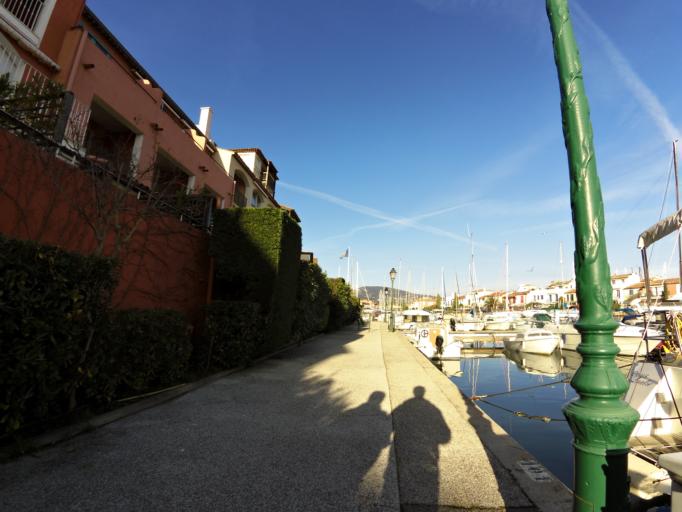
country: FR
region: Provence-Alpes-Cote d'Azur
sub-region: Departement du Var
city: Gassin
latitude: 43.2712
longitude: 6.5743
